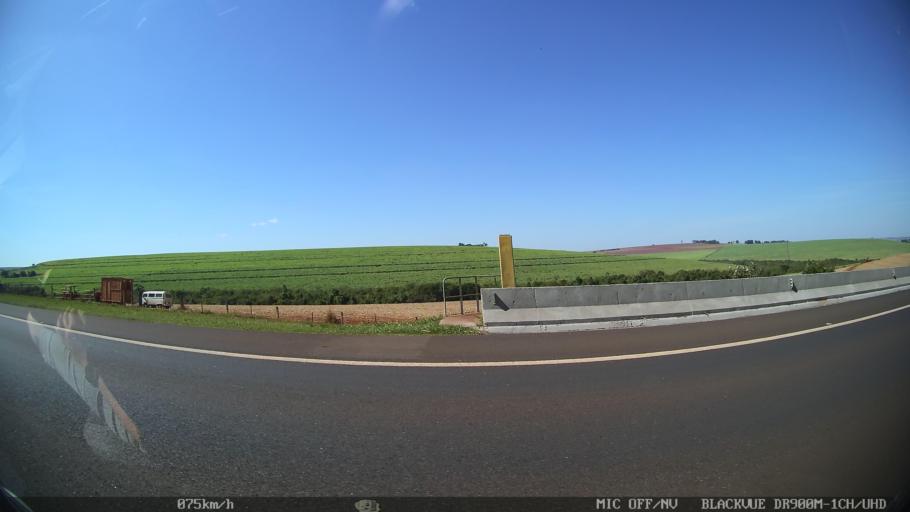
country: BR
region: Sao Paulo
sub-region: Batatais
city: Batatais
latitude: -20.7100
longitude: -47.5045
